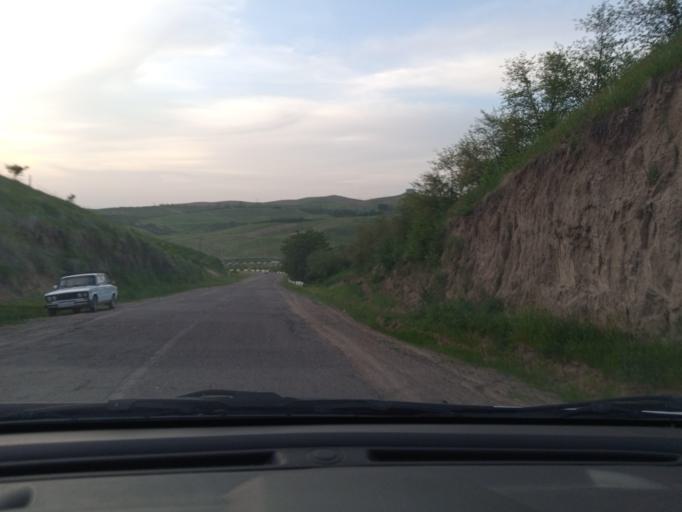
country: UZ
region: Toshkent
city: Parkent
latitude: 41.2392
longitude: 69.7334
